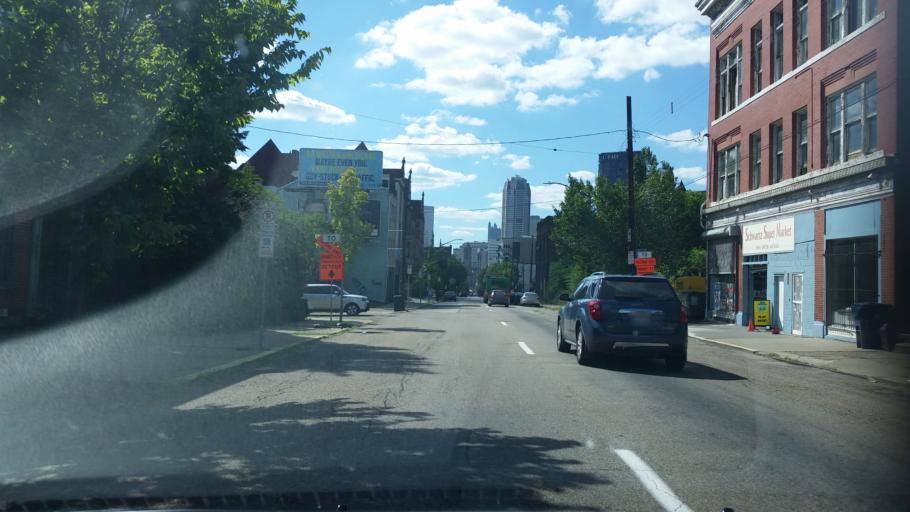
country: US
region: Pennsylvania
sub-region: Allegheny County
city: Pittsburgh
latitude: 40.4383
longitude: -79.9789
